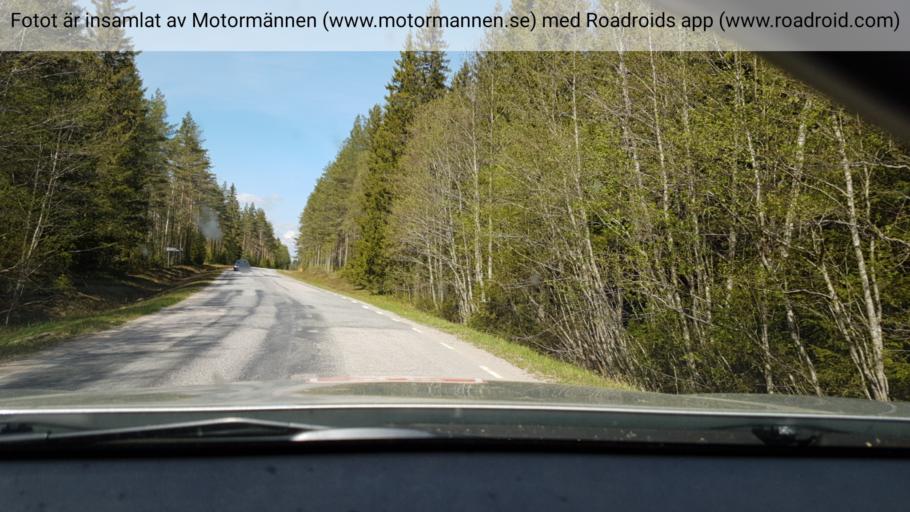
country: SE
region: Vaesterbotten
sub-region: Umea Kommun
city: Saevar
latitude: 63.8443
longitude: 20.6017
